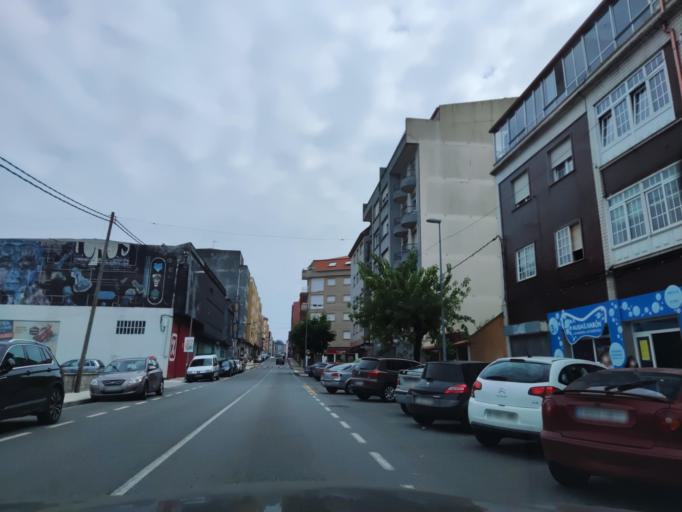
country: ES
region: Galicia
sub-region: Provincia da Coruna
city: Boiro
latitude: 42.6460
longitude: -8.8890
